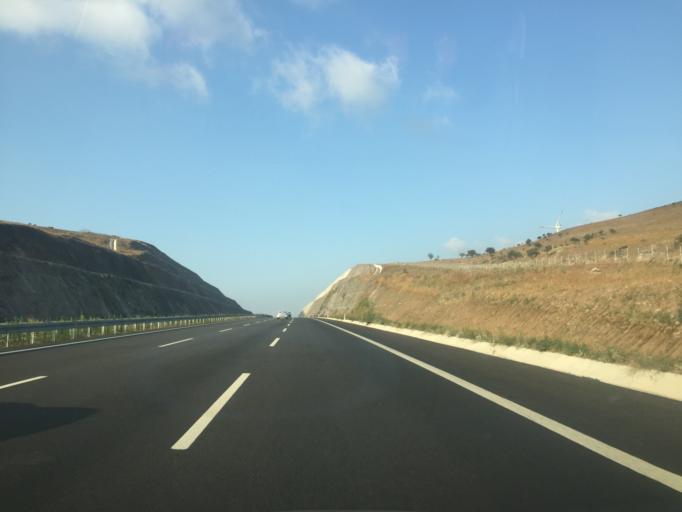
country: TR
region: Balikesir
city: Balikesir
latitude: 39.7035
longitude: 27.7877
